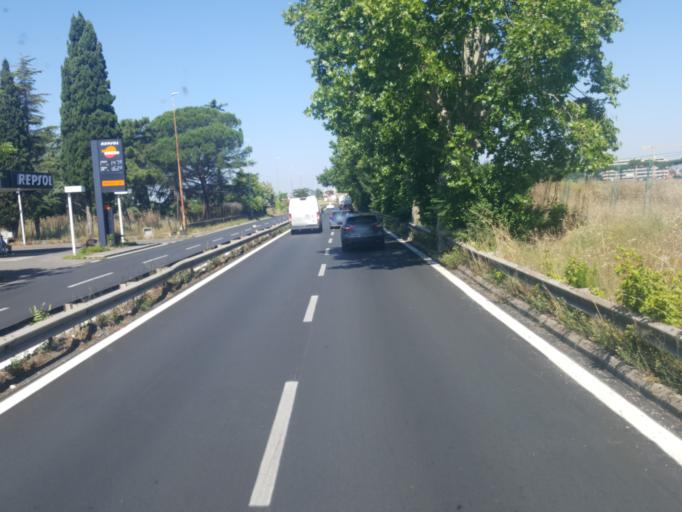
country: IT
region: Latium
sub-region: Citta metropolitana di Roma Capitale
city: Ciampino
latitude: 41.8326
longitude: 12.6134
